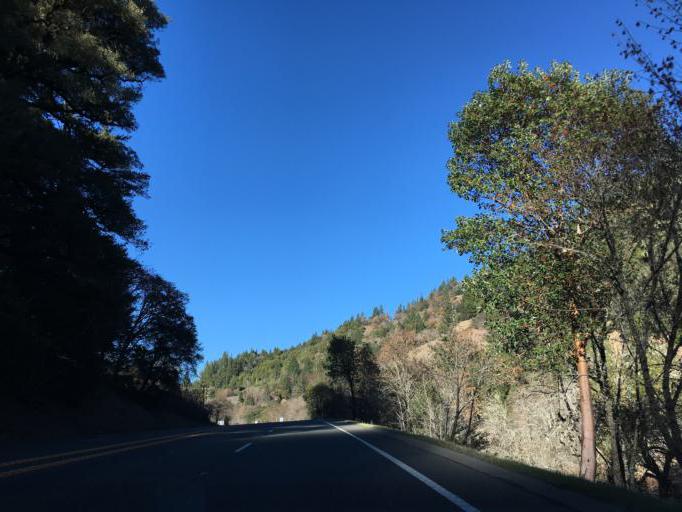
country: US
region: California
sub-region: Mendocino County
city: Brooktrails
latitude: 39.5589
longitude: -123.4328
